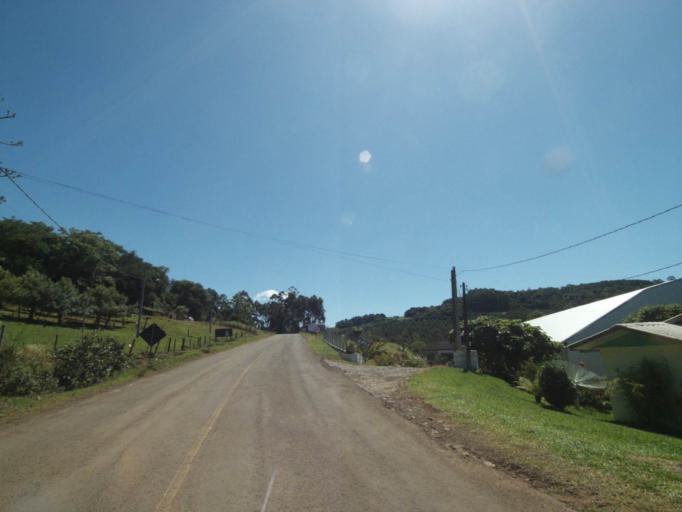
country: BR
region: Parana
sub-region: Ampere
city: Ampere
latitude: -26.1792
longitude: -53.3624
